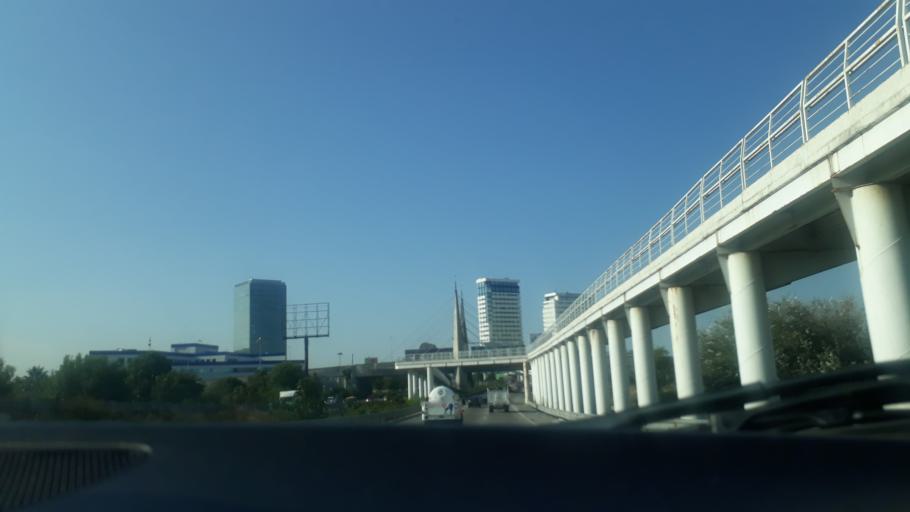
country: MX
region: Puebla
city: Tlazcalancingo
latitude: 19.0145
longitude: -98.2639
